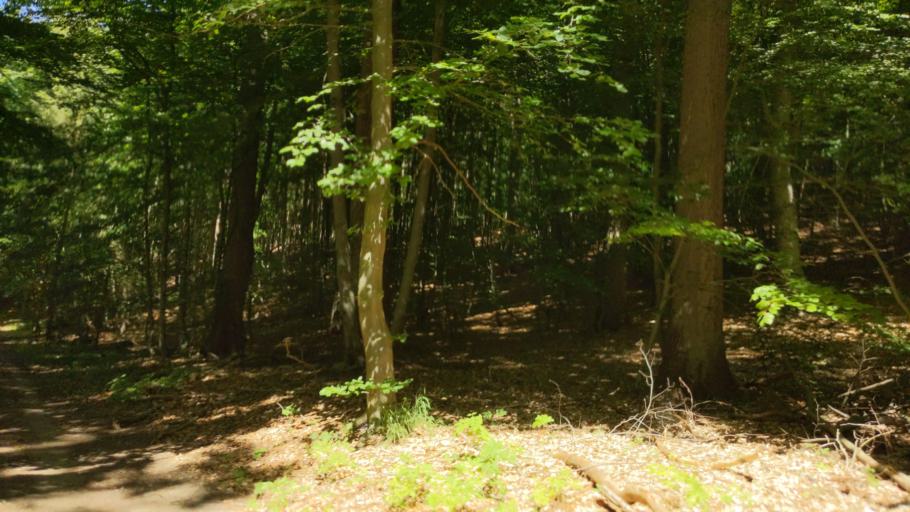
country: DE
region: Schleswig-Holstein
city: Schmilau
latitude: 53.6822
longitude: 10.7620
